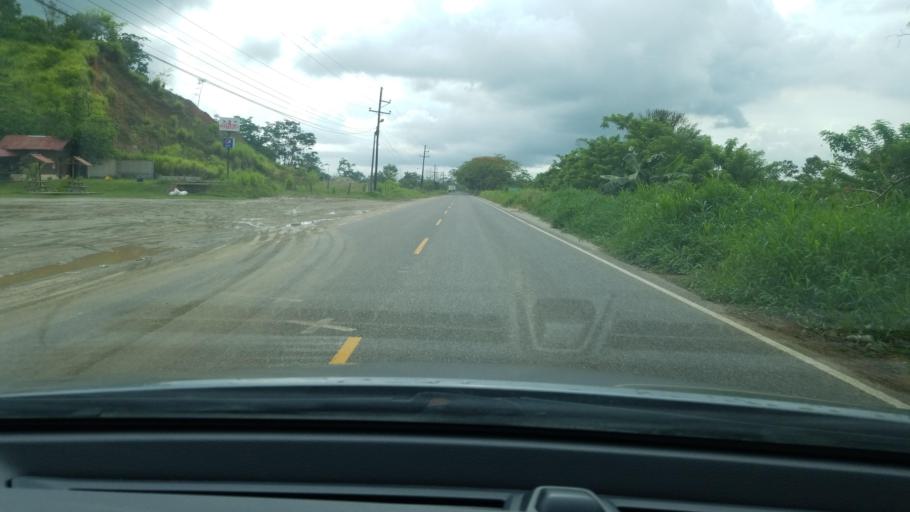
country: HN
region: Cortes
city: Potrerillos
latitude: 15.5951
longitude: -88.3142
